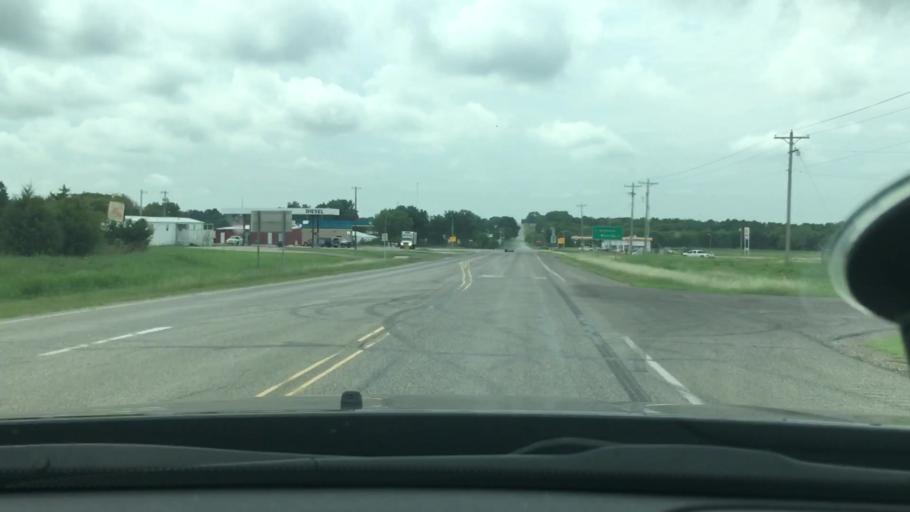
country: US
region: Oklahoma
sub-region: Carter County
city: Wilson
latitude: 34.1753
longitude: -97.4749
